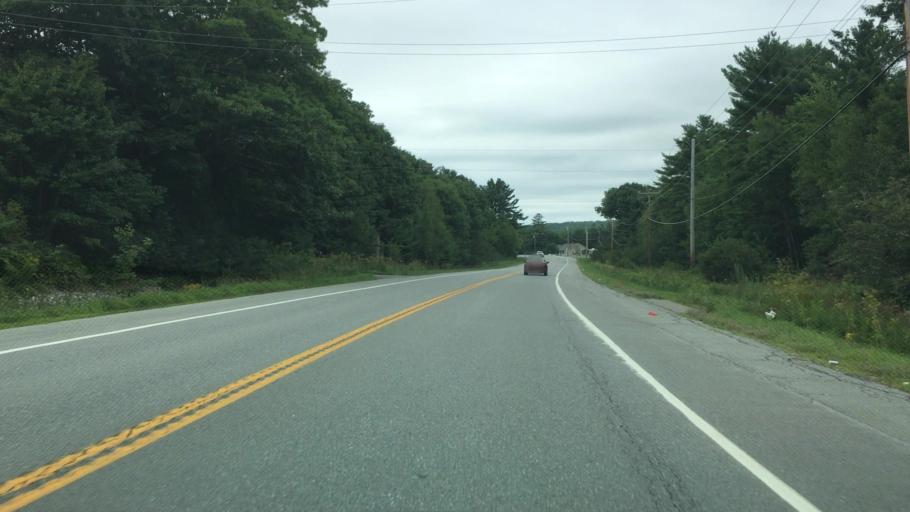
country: US
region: Maine
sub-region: Waldo County
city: Frankfort
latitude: 44.6161
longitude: -68.8697
